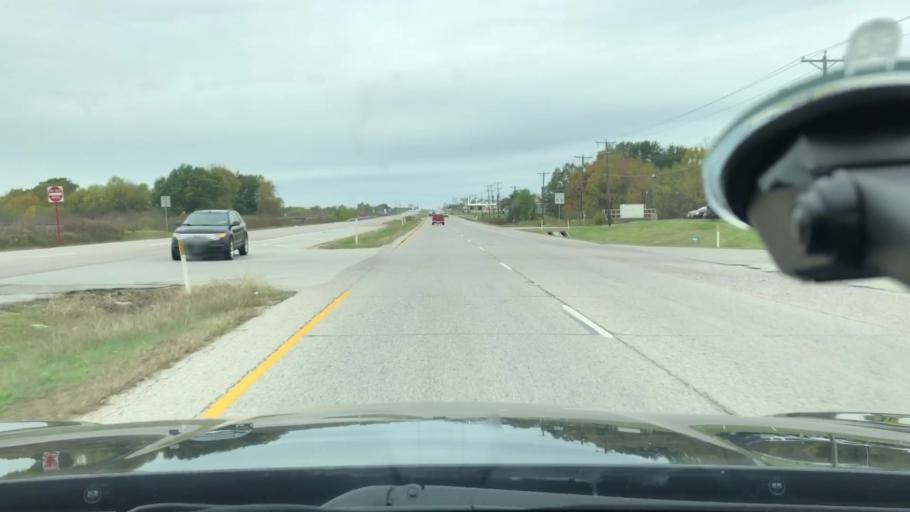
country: US
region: Texas
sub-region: Kaufman County
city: Terrell
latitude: 32.7372
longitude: -96.3067
